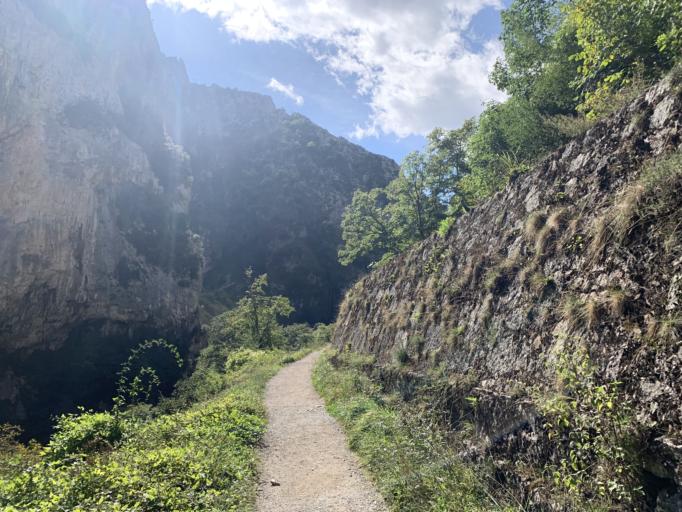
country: ES
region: Castille and Leon
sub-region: Provincia de Leon
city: Posada de Valdeon
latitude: 43.2305
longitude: -4.8942
